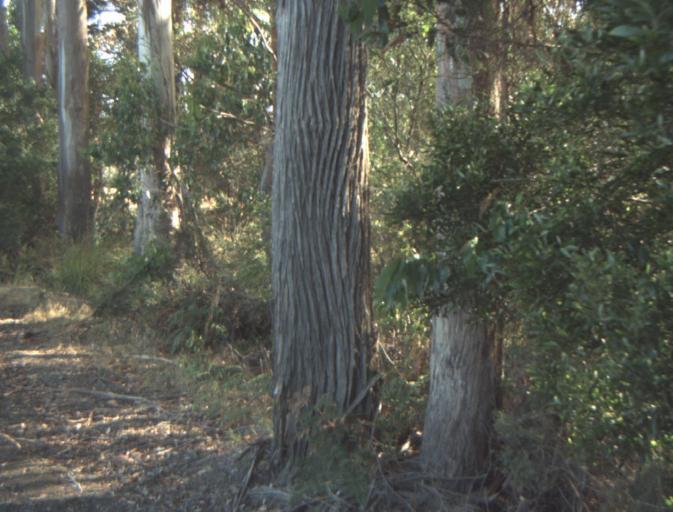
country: AU
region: Tasmania
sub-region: Dorset
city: Bridport
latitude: -41.1570
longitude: 147.2353
